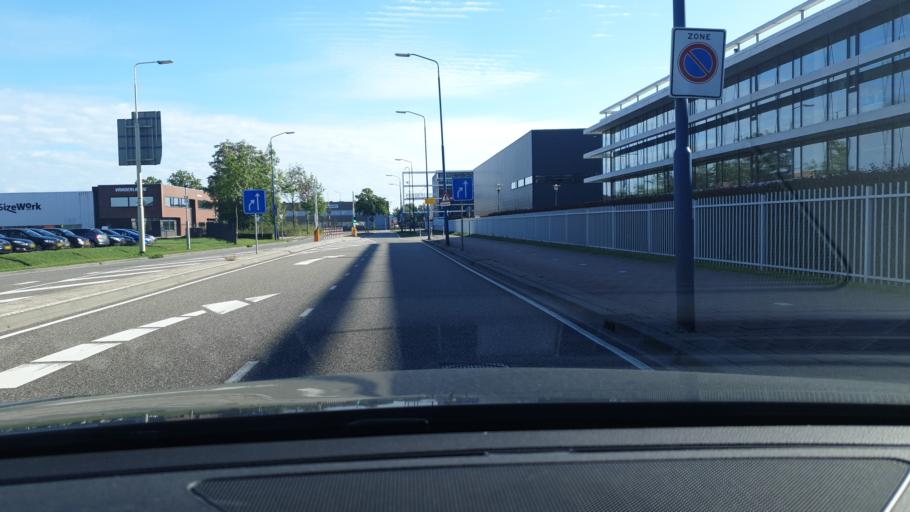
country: NL
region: North Brabant
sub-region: Gemeente Veghel
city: Eerde
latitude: 51.6016
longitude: 5.5153
